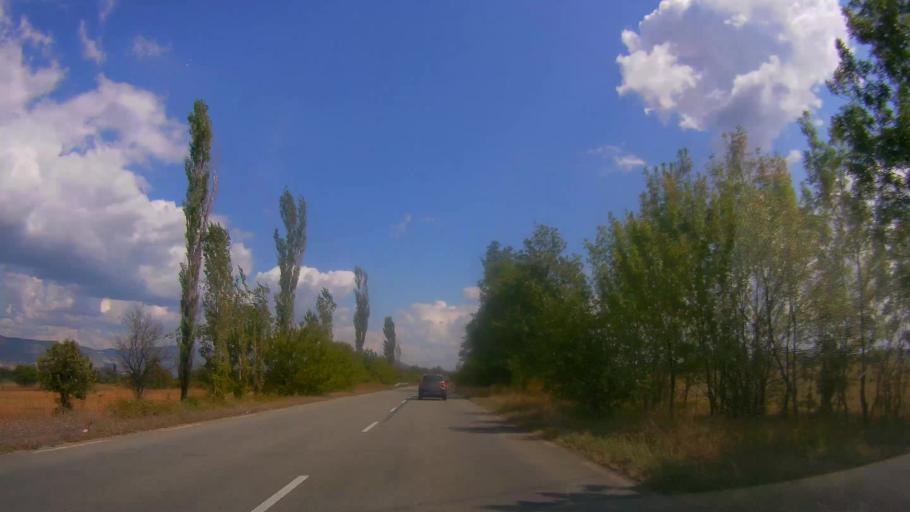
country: BG
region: Sliven
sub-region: Obshtina Tvurditsa
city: Tvurditsa
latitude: 42.6534
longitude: 25.9626
